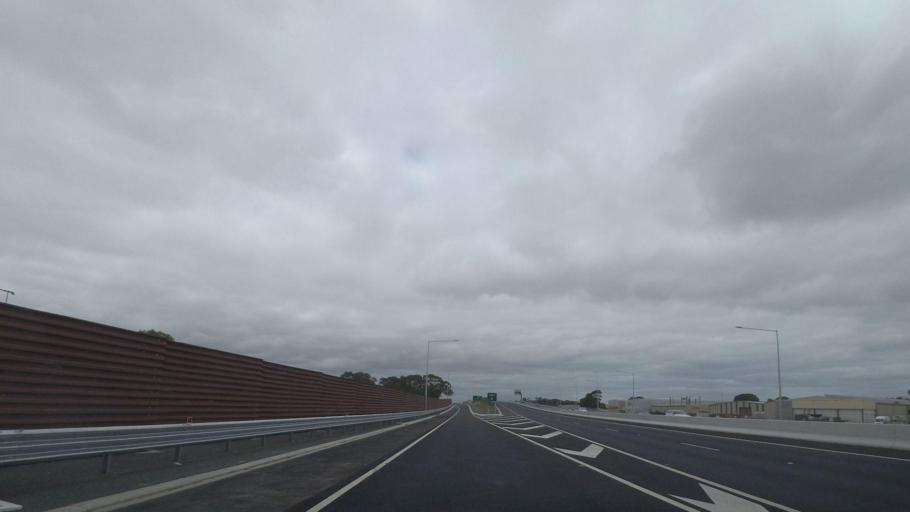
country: AU
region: Victoria
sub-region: Kingston
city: Dingley Village
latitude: -37.9829
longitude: 145.1164
